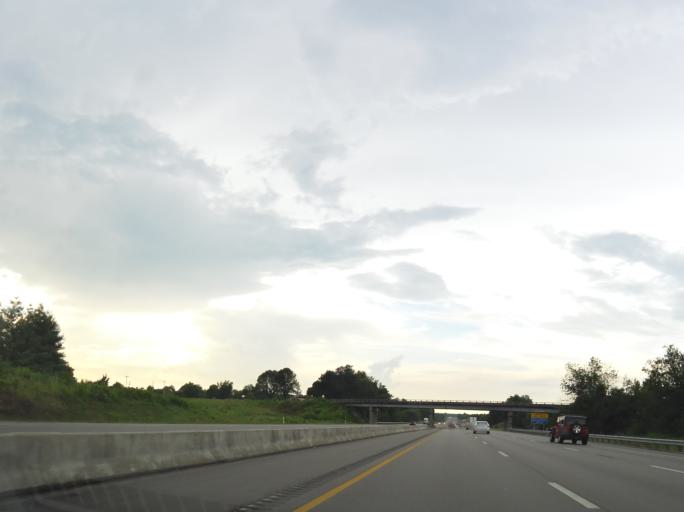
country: US
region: Kentucky
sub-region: Fayette County
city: Lexington
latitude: 37.9234
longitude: -84.3701
